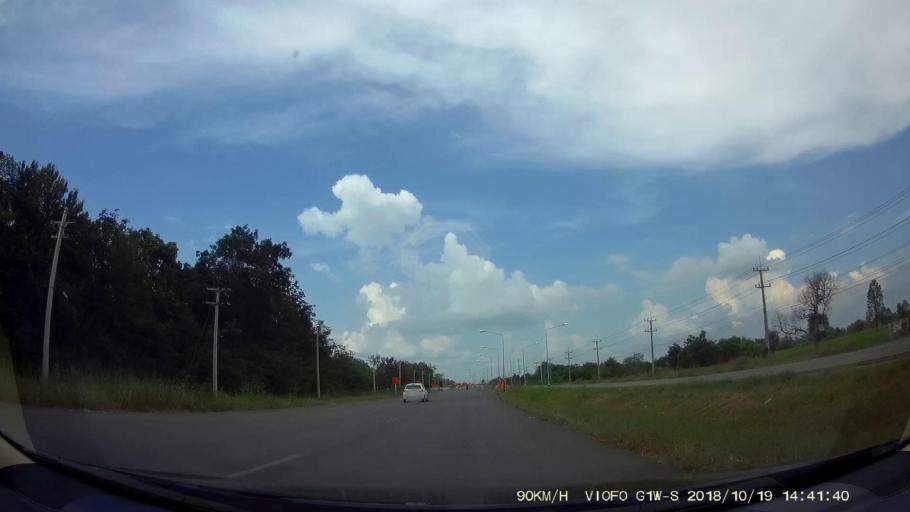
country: TH
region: Chaiyaphum
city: Phu Khiao
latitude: 16.2603
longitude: 102.2000
